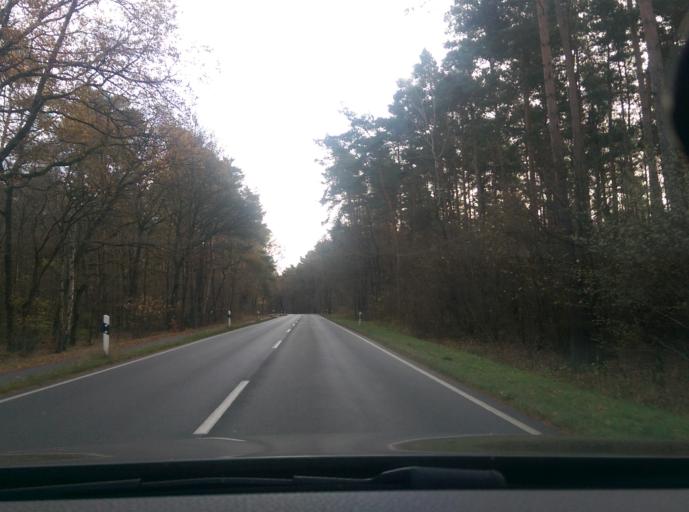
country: DE
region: Lower Saxony
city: Hambuhren
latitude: 52.6477
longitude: 10.0094
